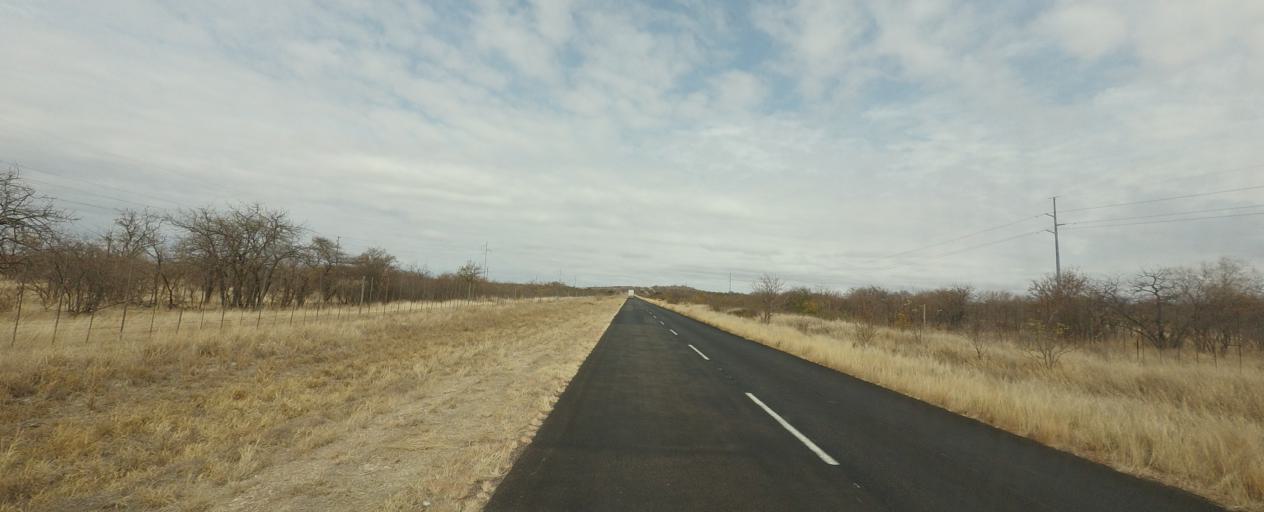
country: ZW
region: Matabeleland South
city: Beitbridge
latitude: -22.4303
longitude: 29.4105
